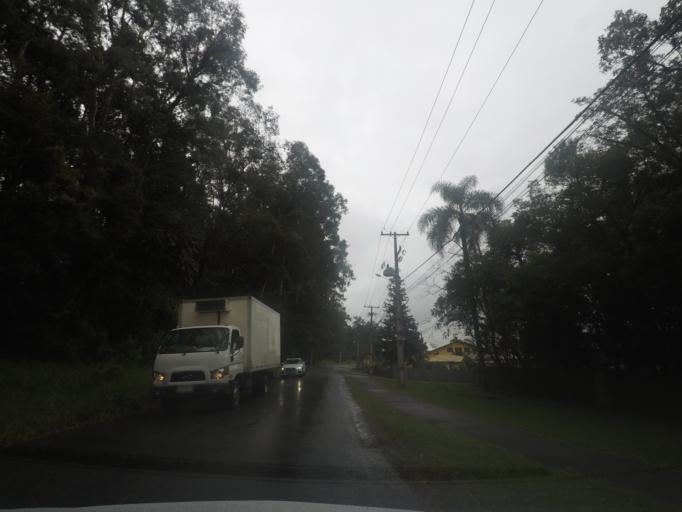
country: BR
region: Parana
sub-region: Quatro Barras
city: Quatro Barras
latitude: -25.3823
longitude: -49.1306
